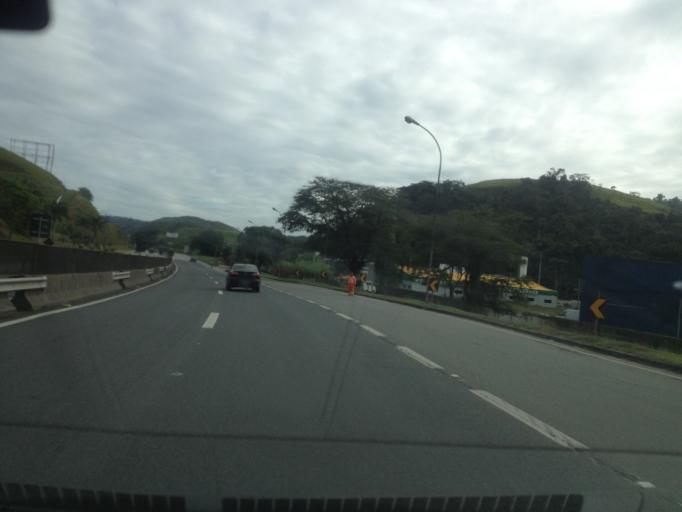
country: BR
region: Rio de Janeiro
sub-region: Pirai
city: Pirai
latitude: -22.6353
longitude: -43.9024
